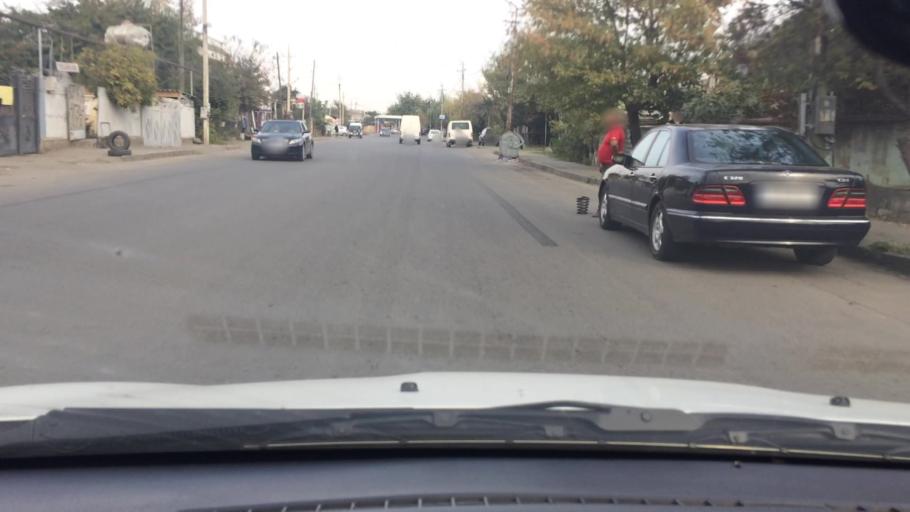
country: GE
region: Kvemo Kartli
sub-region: Marneuli
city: Marneuli
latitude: 41.4638
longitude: 44.8129
